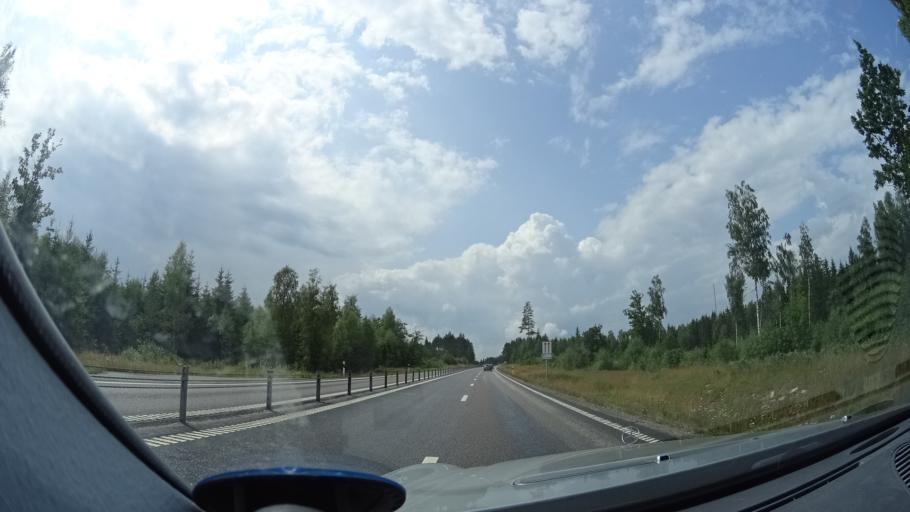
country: SE
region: Kalmar
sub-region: Nybro Kommun
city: Nybro
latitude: 56.7251
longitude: 15.8179
